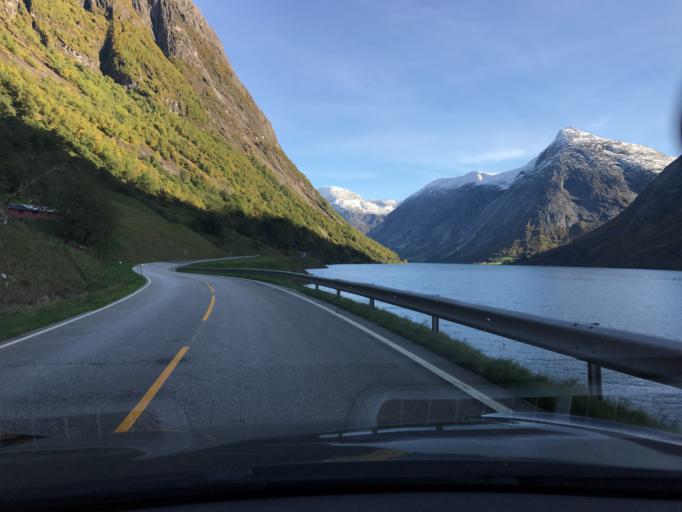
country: NO
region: Sogn og Fjordane
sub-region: Jolster
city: Skei
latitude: 61.5433
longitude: 6.5238
